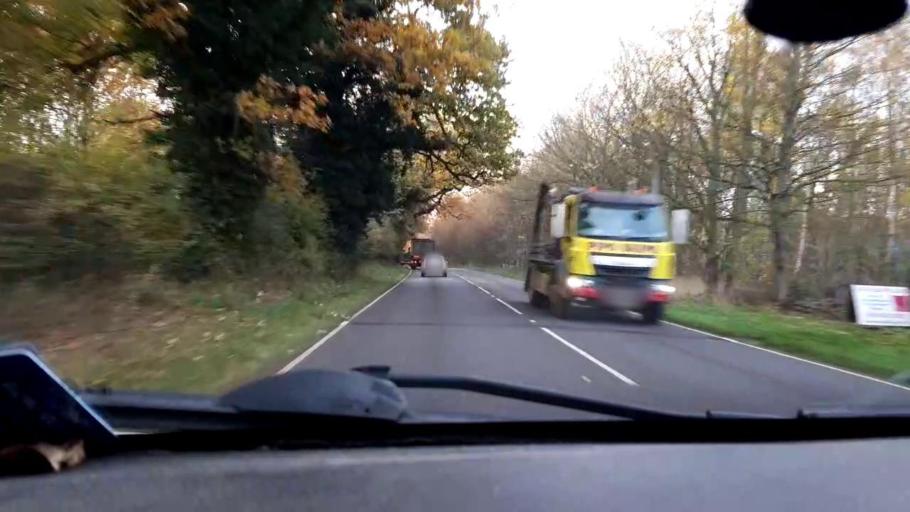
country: GB
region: England
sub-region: Norfolk
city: Costessey
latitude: 52.7184
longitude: 1.1239
